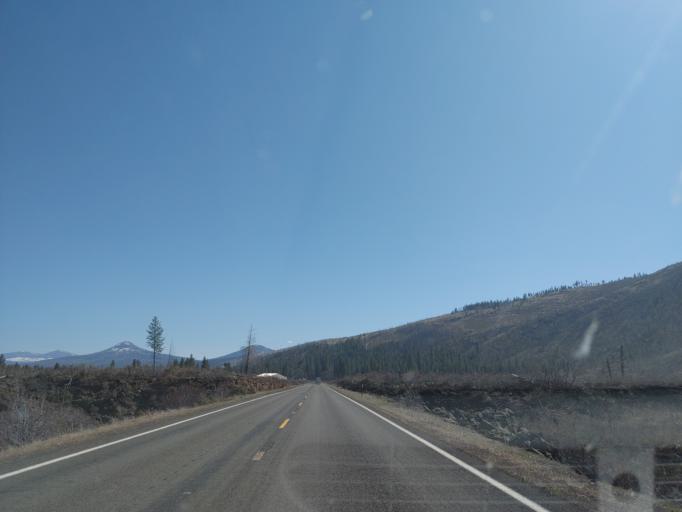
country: US
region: California
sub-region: Shasta County
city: Burney
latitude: 40.8133
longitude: -121.5135
